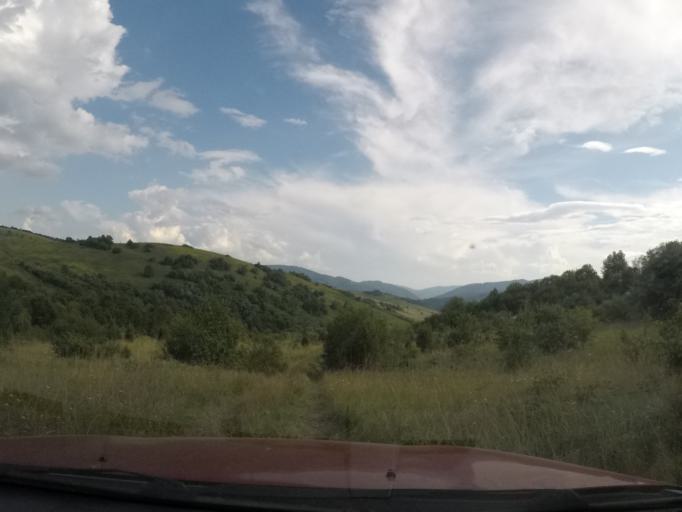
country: PL
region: Subcarpathian Voivodeship
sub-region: Powiat bieszczadzki
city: Lutowiska
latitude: 49.0346
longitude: 22.6391
